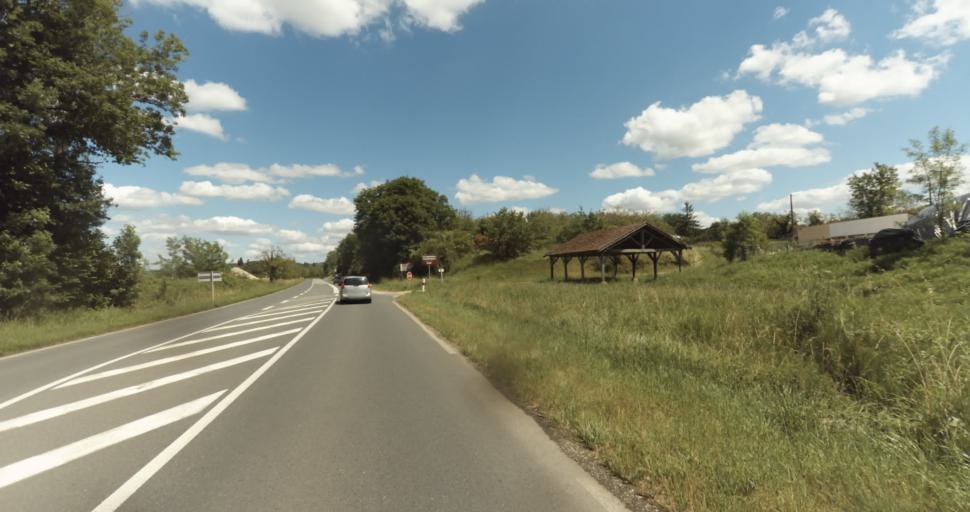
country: FR
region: Aquitaine
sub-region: Departement de la Dordogne
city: Belves
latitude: 44.8212
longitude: 0.9676
